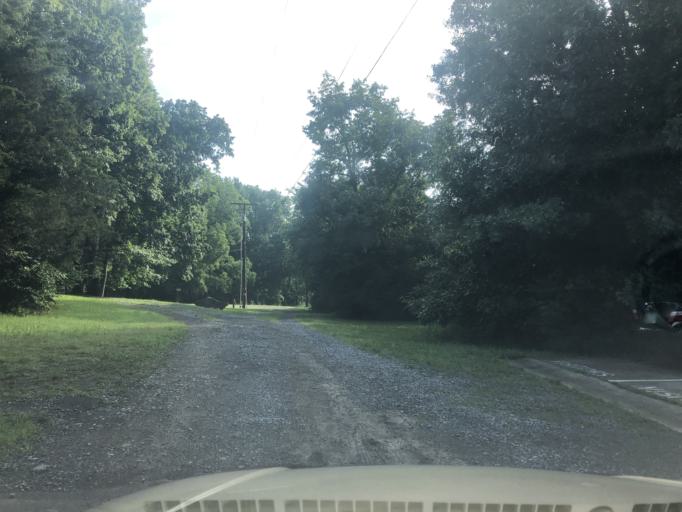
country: US
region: Tennessee
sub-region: Davidson County
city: Lakewood
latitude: 36.2470
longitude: -86.7085
